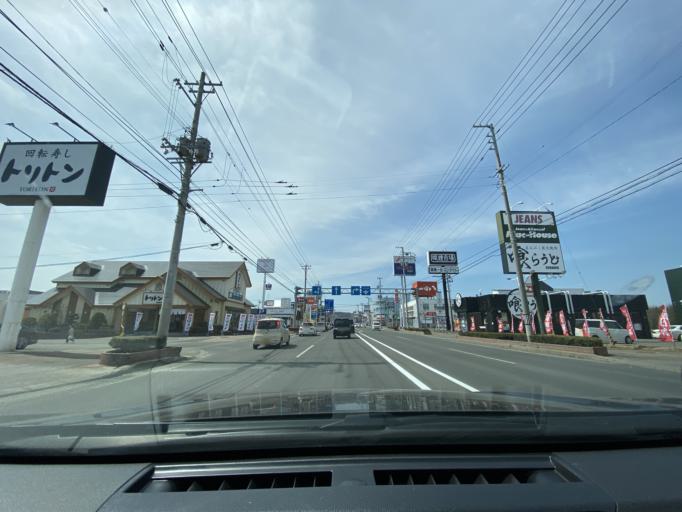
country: JP
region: Hokkaido
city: Kitami
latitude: 43.7980
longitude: 143.8588
